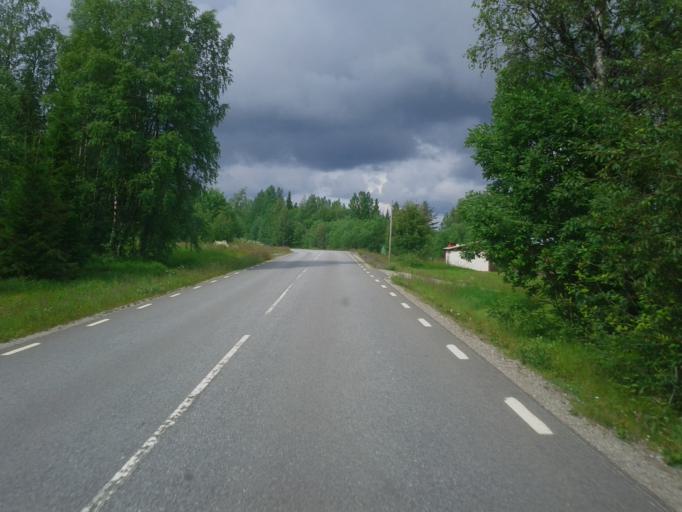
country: SE
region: Vaesterbotten
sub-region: Norsjo Kommun
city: Norsjoe
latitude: 65.0175
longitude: 19.1341
